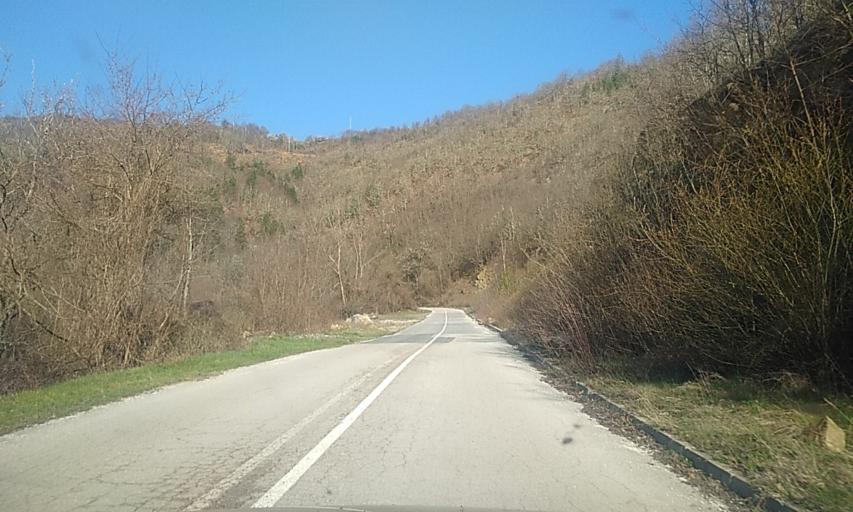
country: RS
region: Central Serbia
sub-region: Pcinjski Okrug
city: Bosilegrad
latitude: 42.3995
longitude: 22.4604
